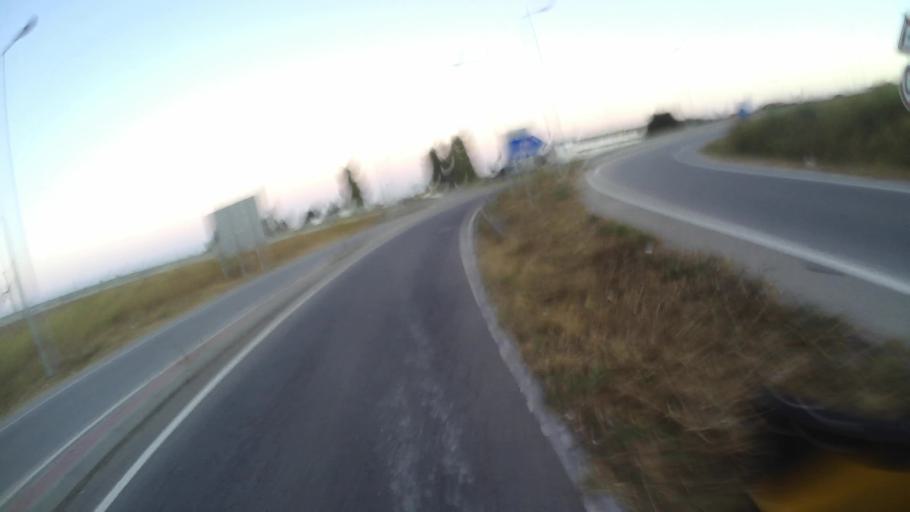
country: PT
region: Aveiro
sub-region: Ilhavo
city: Gafanha da Nazare
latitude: 40.6313
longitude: -8.6890
